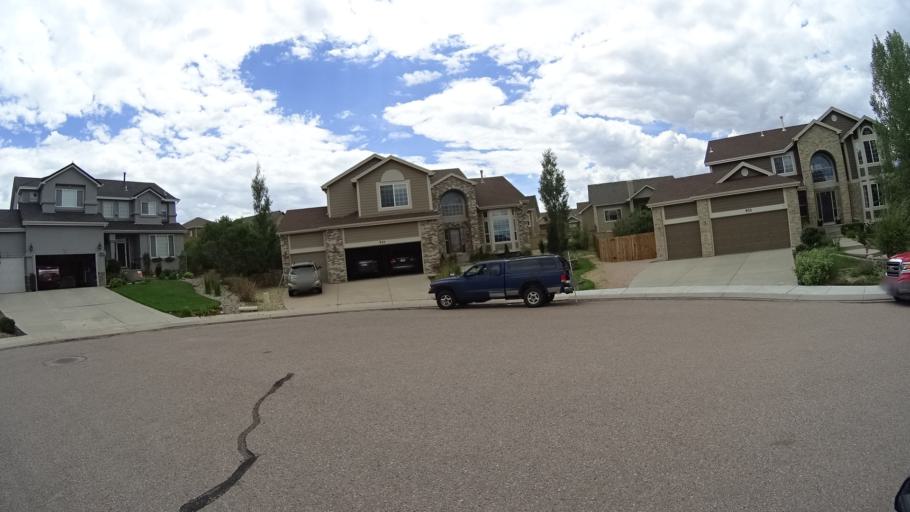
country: US
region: Colorado
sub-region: El Paso County
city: Gleneagle
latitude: 39.0317
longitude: -104.8118
